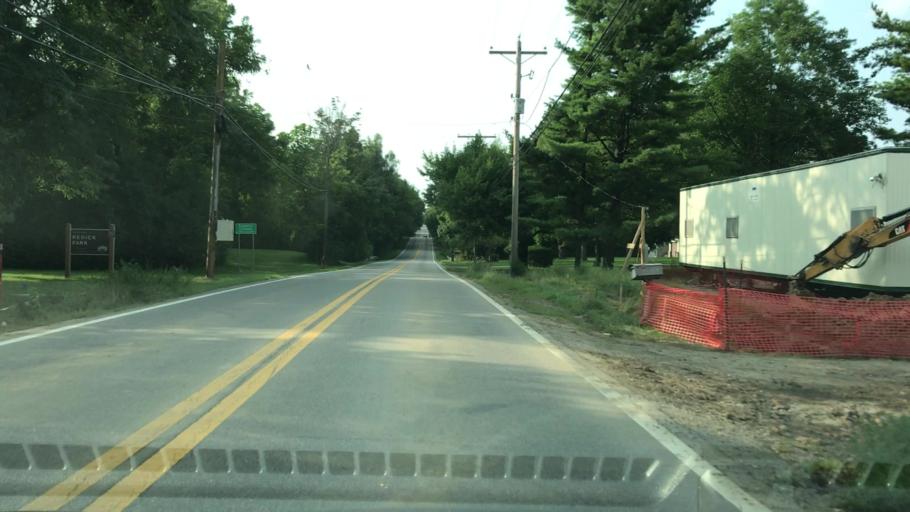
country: US
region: Ohio
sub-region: Franklin County
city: Upper Arlington
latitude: 39.9809
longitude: -83.0860
